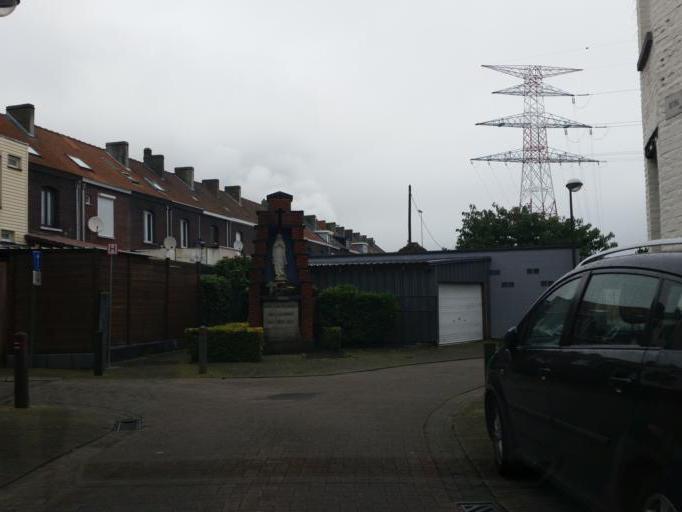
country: BE
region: Flanders
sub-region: Provincie Vlaams-Brabant
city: Drogenbos
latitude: 50.7941
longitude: 4.2982
